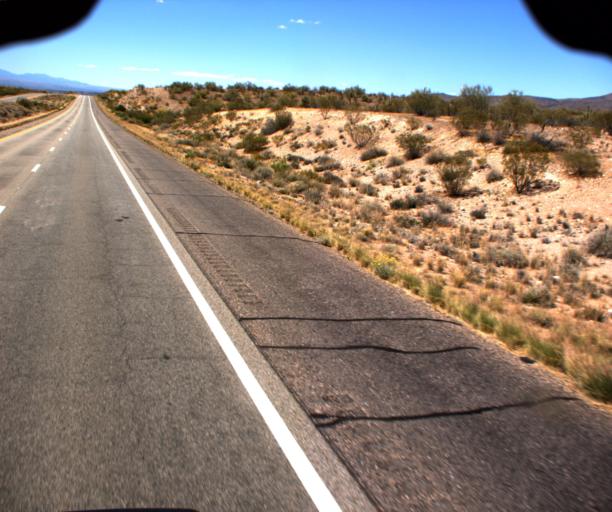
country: US
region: Arizona
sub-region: Yavapai County
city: Bagdad
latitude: 34.6044
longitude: -113.5211
